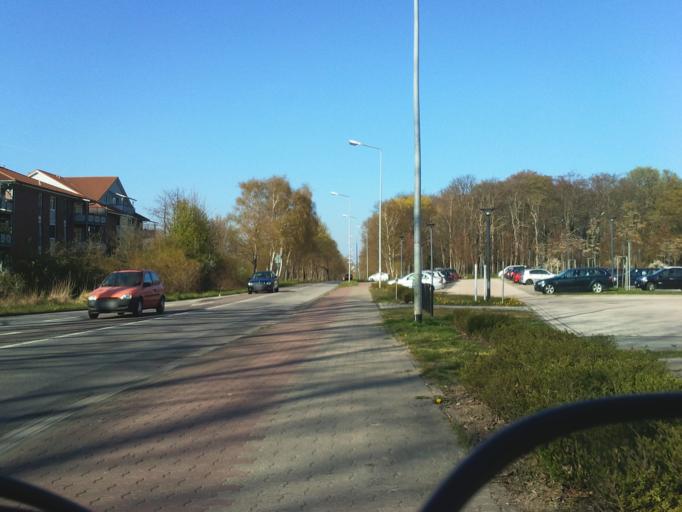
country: DE
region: Mecklenburg-Vorpommern
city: Rostock
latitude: 54.1025
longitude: 12.1310
